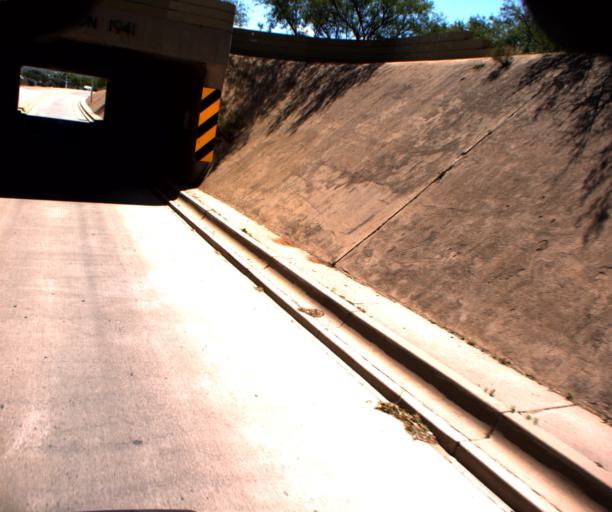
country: US
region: Arizona
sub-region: Cochise County
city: Benson
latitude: 31.9665
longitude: -110.2903
